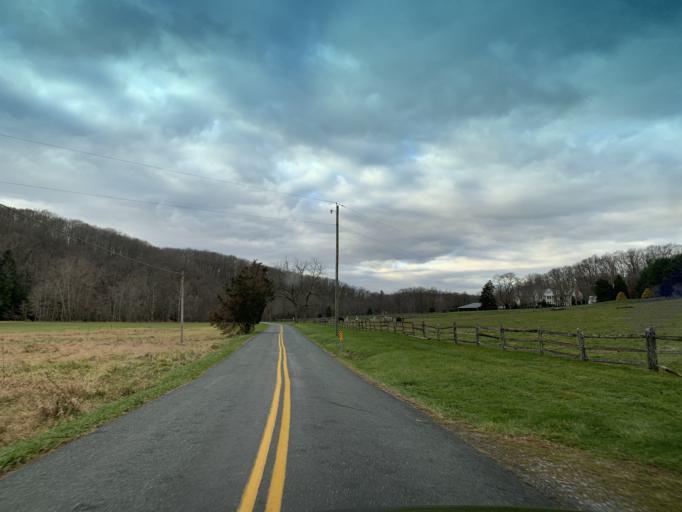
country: US
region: Maryland
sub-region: Harford County
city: Jarrettsville
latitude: 39.6491
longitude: -76.4322
